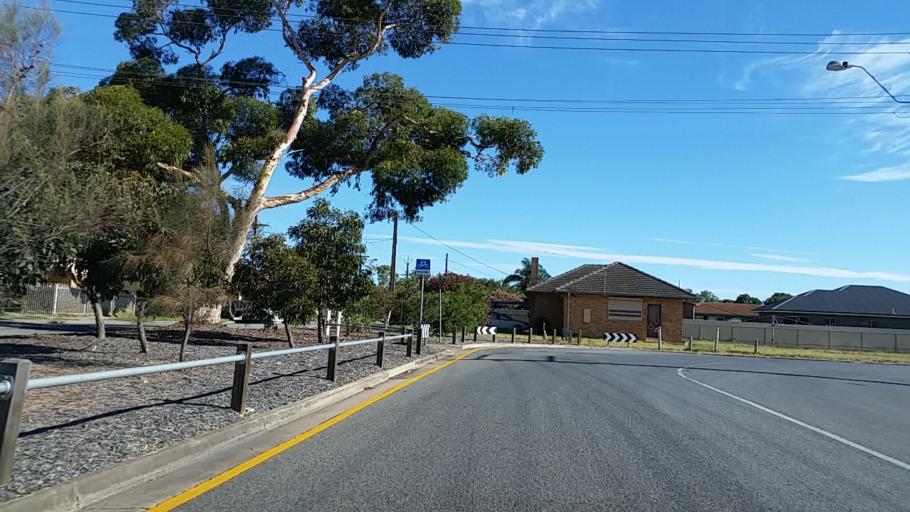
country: AU
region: South Australia
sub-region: Charles Sturt
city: Royal Park
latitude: -34.8680
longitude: 138.5075
